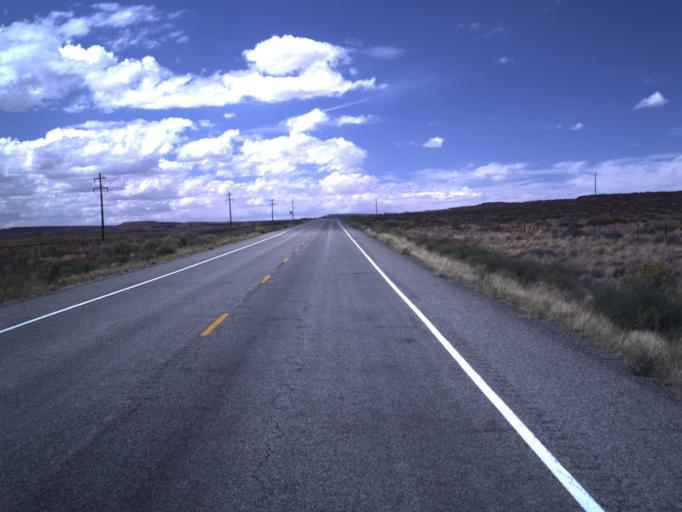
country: US
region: Utah
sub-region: San Juan County
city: Blanding
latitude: 37.2649
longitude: -109.6330
